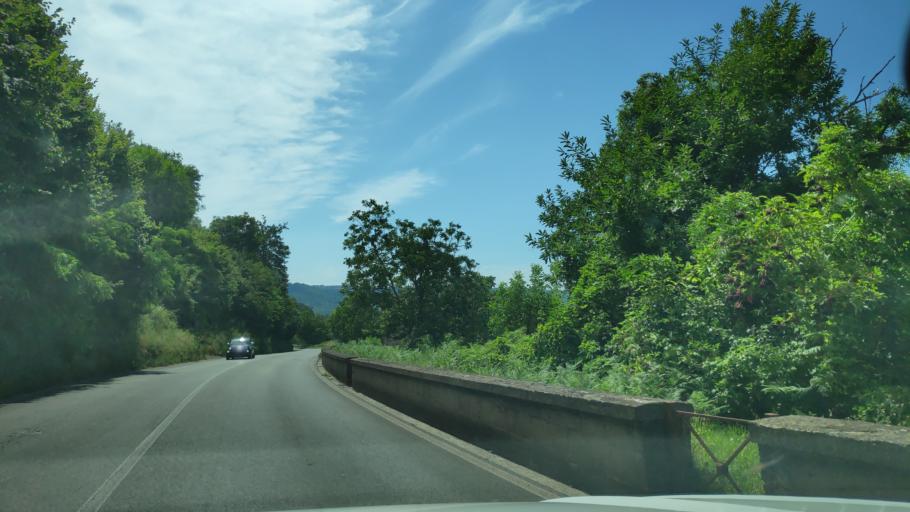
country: IT
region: Umbria
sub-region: Provincia di Terni
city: Orvieto
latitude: 42.7226
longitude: 12.1118
